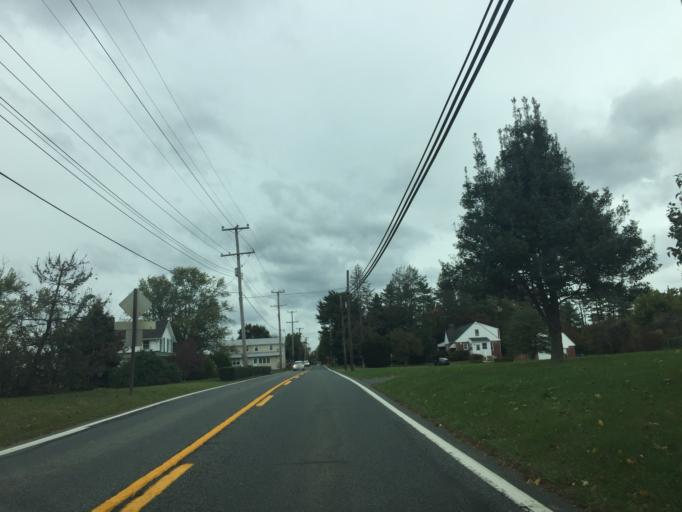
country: US
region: Maryland
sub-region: Harford County
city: Riverside
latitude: 39.5481
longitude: -76.2526
